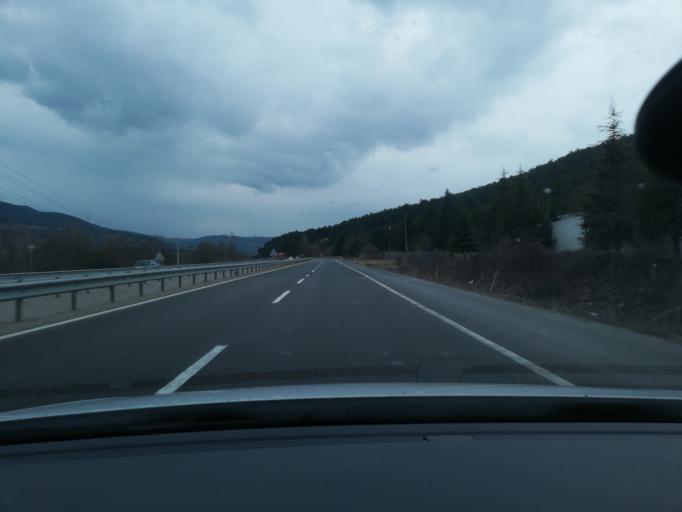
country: TR
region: Bolu
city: Yenicaga
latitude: 40.7448
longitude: 31.8573
